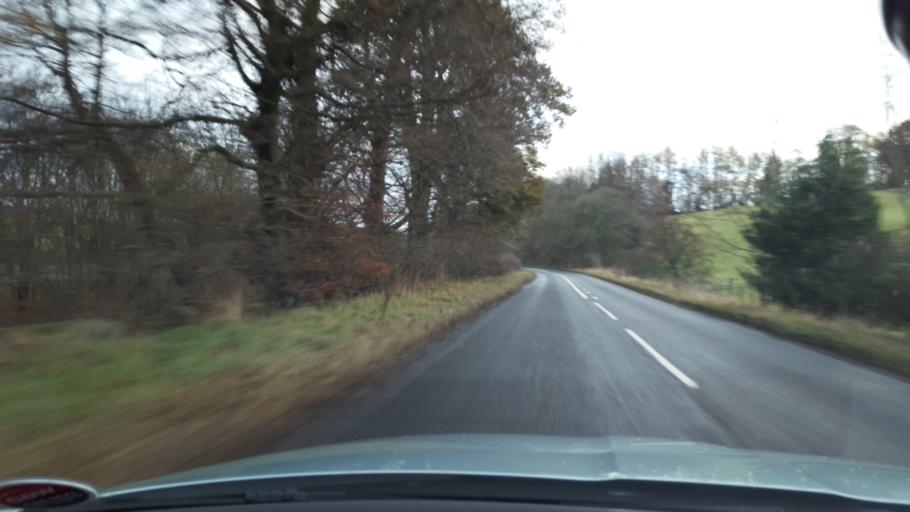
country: GB
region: Scotland
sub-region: Perth and Kinross
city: Milnathort
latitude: 56.2715
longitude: -3.3920
